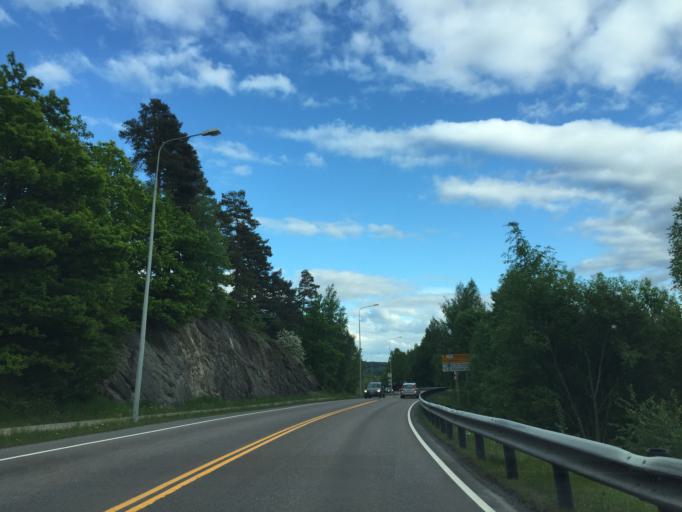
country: NO
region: Akershus
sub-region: Fet
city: Fetsund
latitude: 59.9267
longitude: 11.1521
